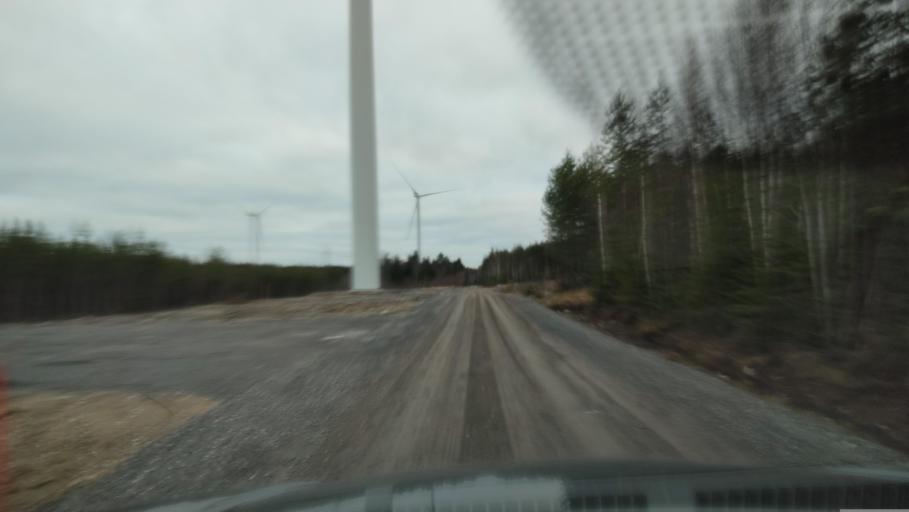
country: FI
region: Southern Ostrobothnia
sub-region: Suupohja
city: Karijoki
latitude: 62.2072
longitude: 21.5995
